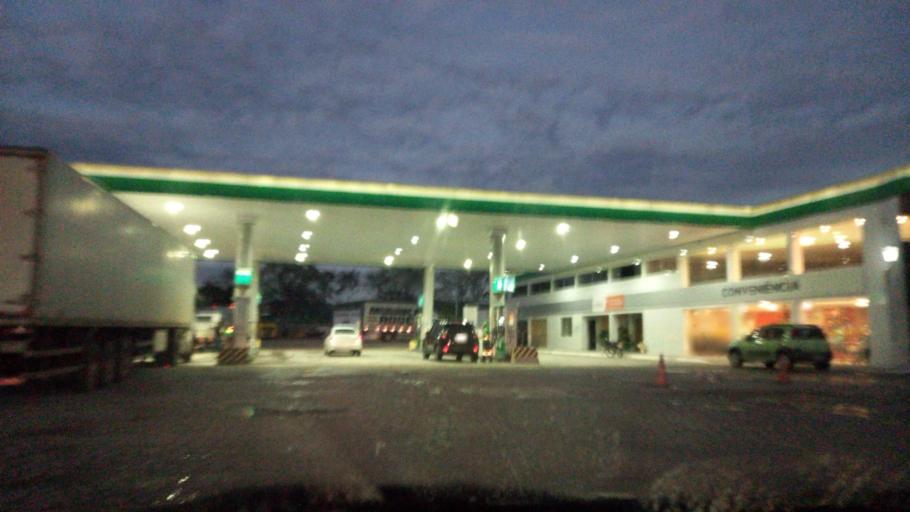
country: BR
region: Pernambuco
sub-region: Escada
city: Escada
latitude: -8.4089
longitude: -35.2785
